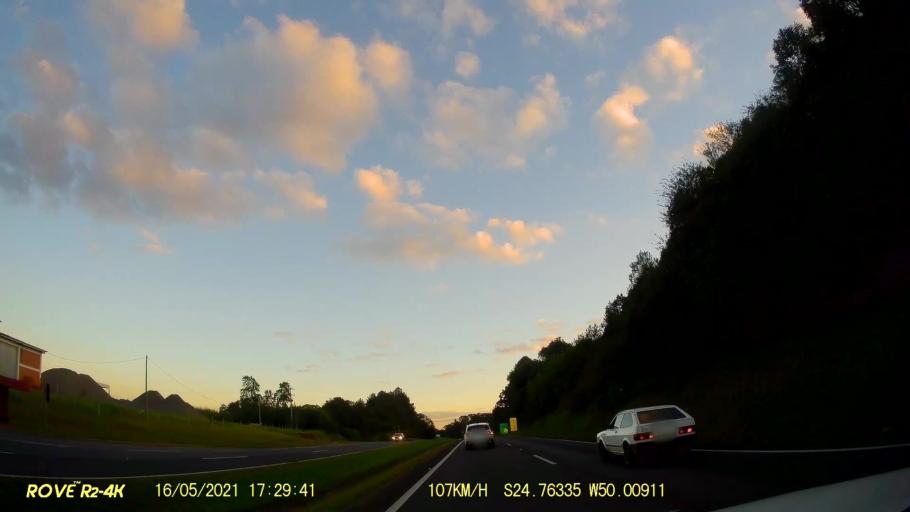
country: BR
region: Parana
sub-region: Castro
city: Castro
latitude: -24.7636
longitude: -50.0093
